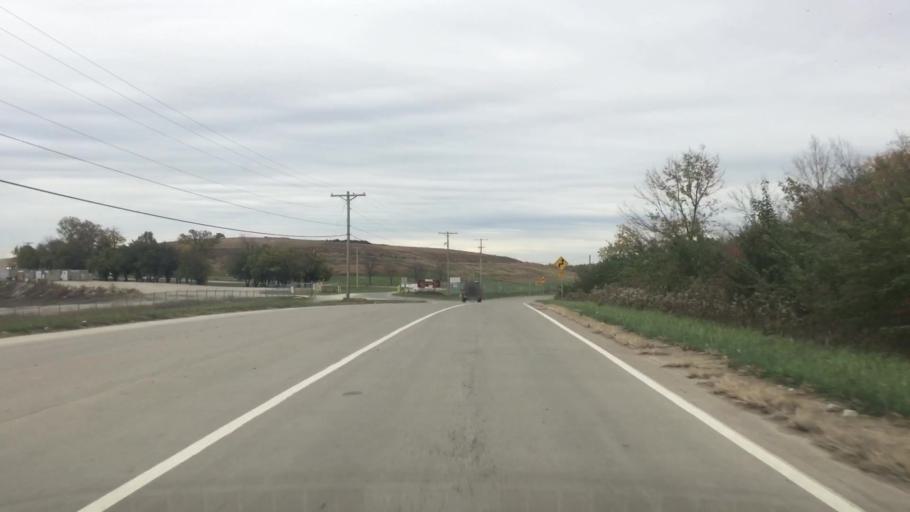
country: US
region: Missouri
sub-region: Jackson County
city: Greenwood
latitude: 38.8825
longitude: -94.3582
